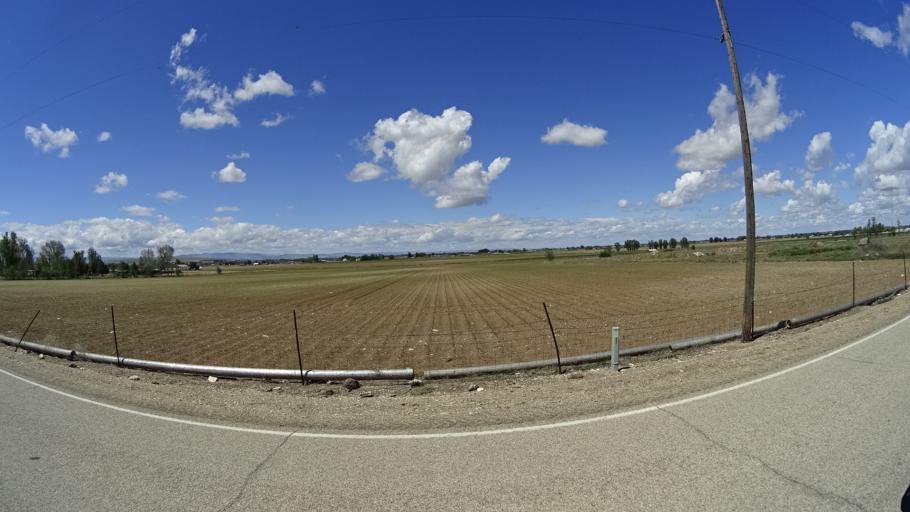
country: US
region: Idaho
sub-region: Ada County
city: Kuna
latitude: 43.4928
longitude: -116.3539
